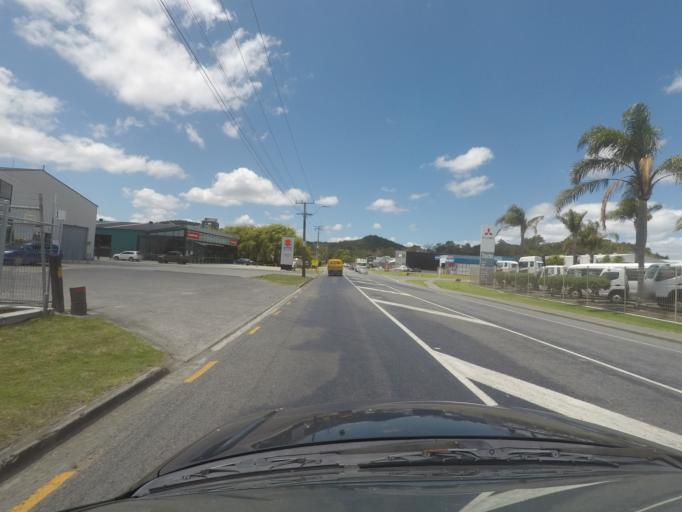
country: NZ
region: Northland
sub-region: Whangarei
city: Whangarei
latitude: -35.7521
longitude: 174.3156
